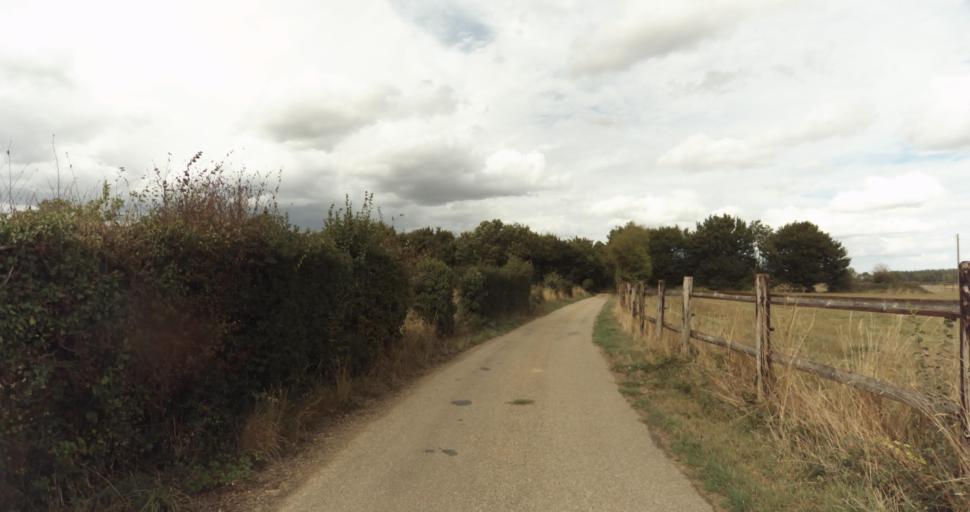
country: FR
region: Lower Normandy
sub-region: Departement de l'Orne
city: Gace
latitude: 48.8860
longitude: 0.3620
